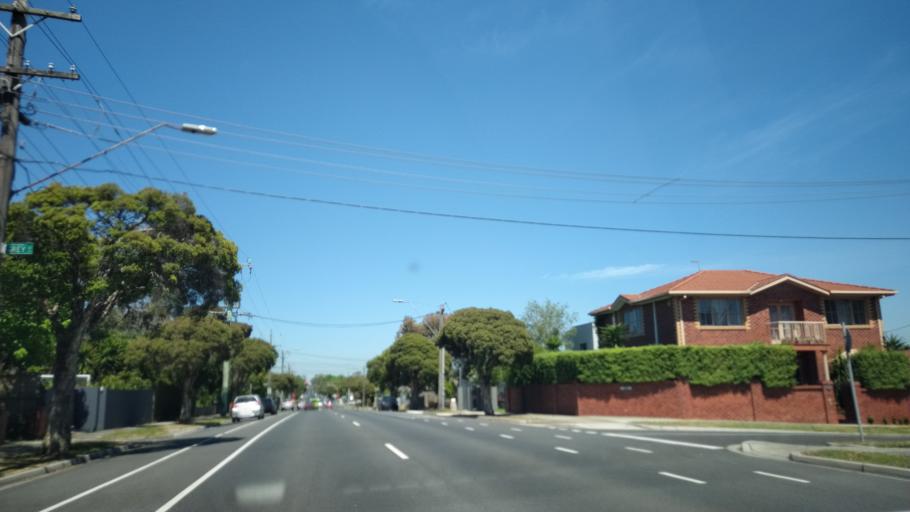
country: AU
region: Victoria
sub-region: Glen Eira
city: Caulfield South
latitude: -37.9002
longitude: 145.0264
